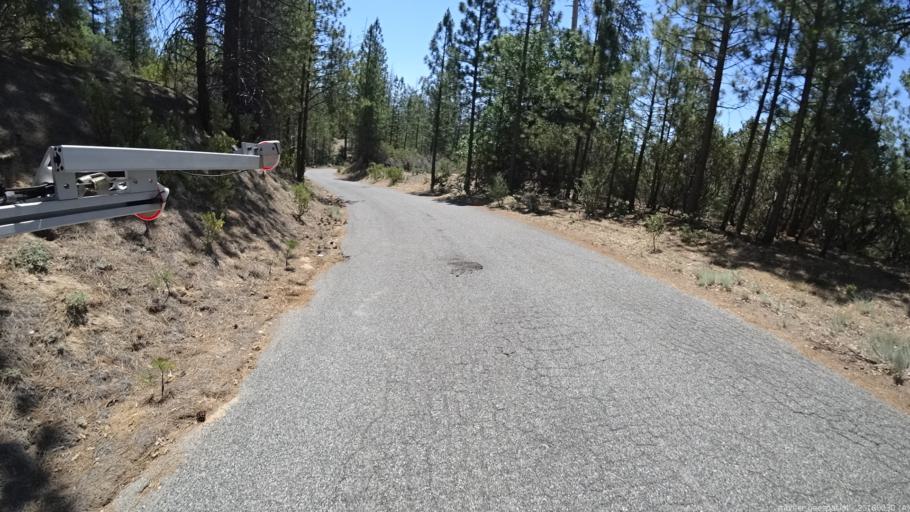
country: US
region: California
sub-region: Madera County
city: Oakhurst
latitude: 37.3758
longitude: -119.3591
